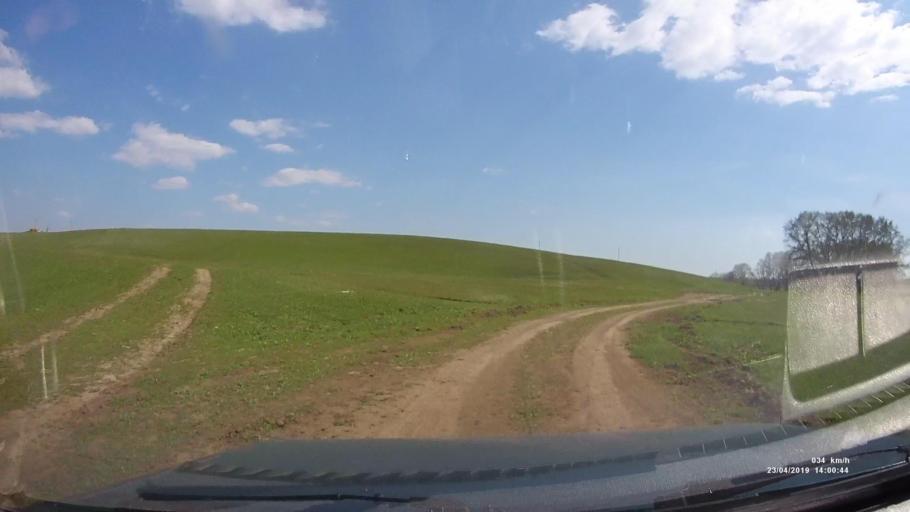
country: RU
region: Rostov
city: Remontnoye
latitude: 46.5581
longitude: 42.9471
